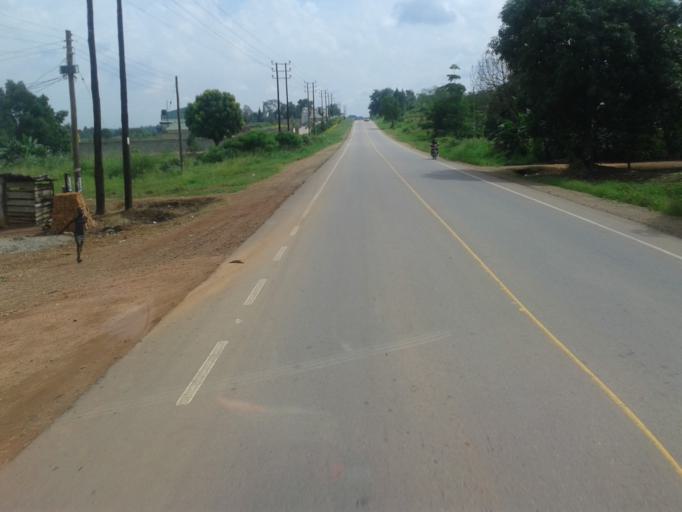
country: UG
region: Central Region
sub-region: Wakiso District
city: Wakiso
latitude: 0.5357
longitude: 32.5305
